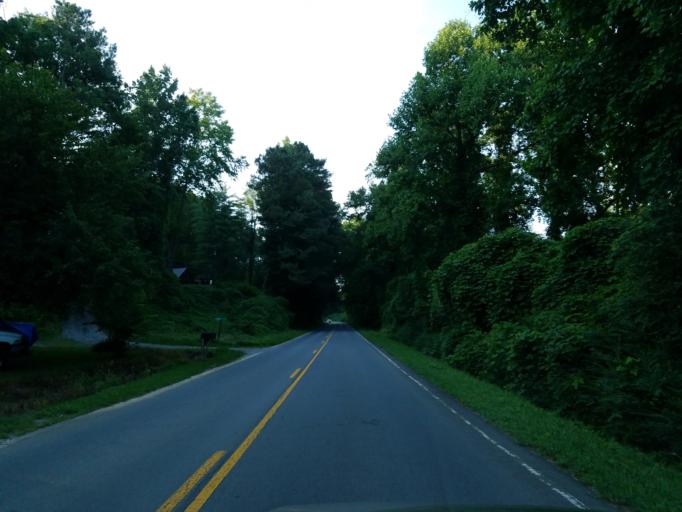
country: US
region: Georgia
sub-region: Gilmer County
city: Ellijay
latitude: 34.5996
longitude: -84.5282
